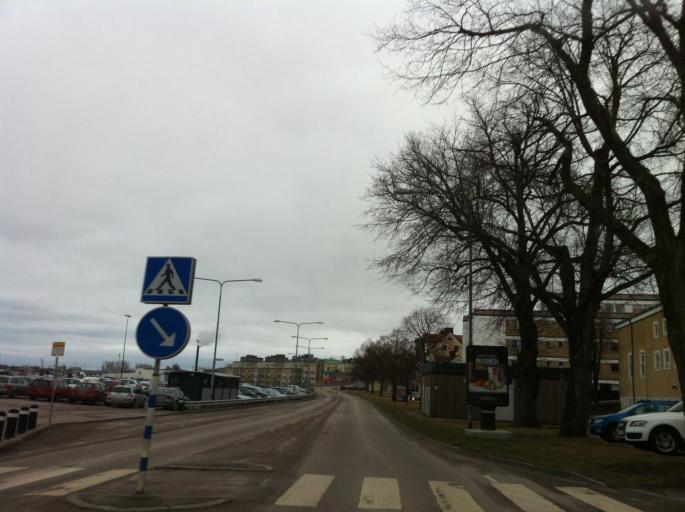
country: SE
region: Kalmar
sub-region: Vasterviks Kommun
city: Vaestervik
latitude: 57.7988
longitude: 16.6138
